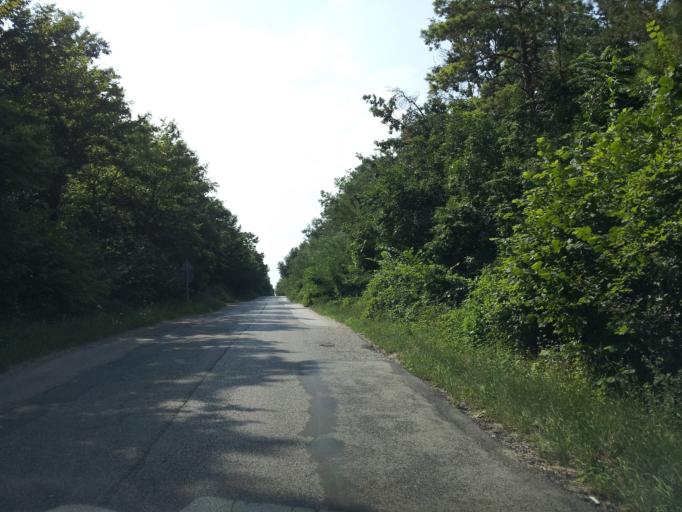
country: HU
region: Veszprem
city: Balatonfured
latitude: 46.9639
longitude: 17.8548
